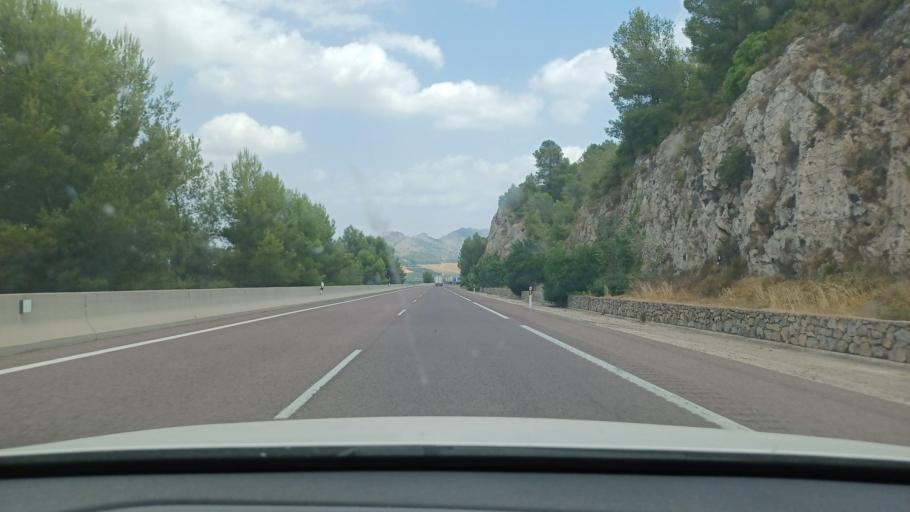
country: ES
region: Valencia
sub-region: Provincia de Valencia
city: L'Olleria
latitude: 38.9342
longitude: -0.5721
